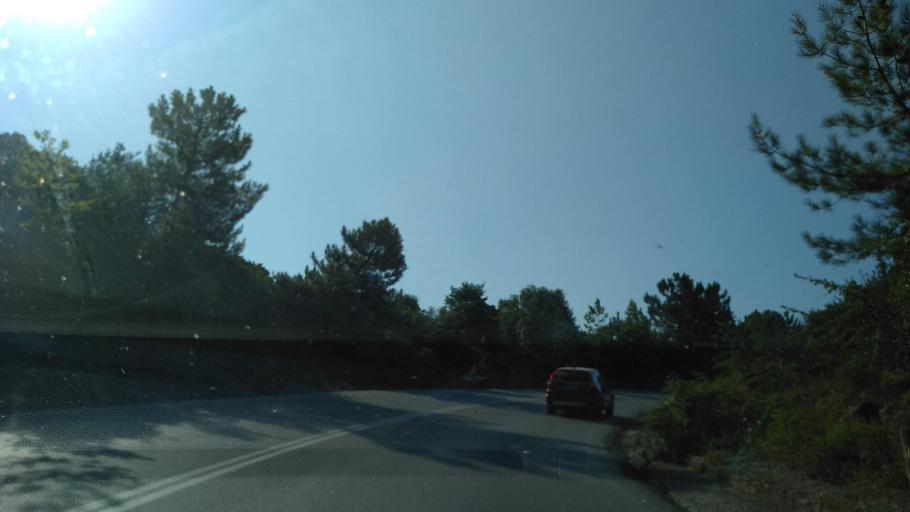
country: GR
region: Central Macedonia
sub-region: Nomos Chalkidikis
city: Stratonion
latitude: 40.5700
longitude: 23.8209
